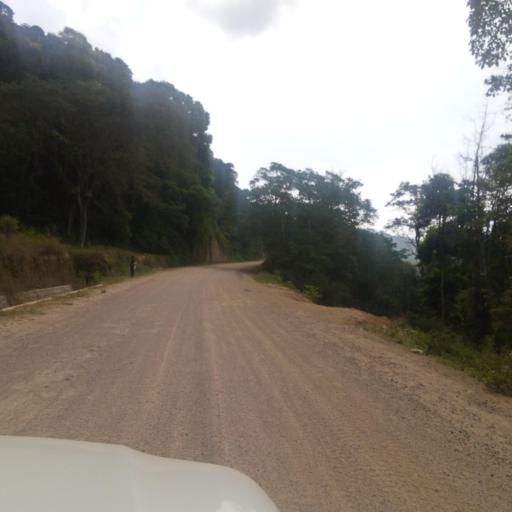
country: ET
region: Southern Nations, Nationalities, and People's Region
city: Tippi
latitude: 7.0486
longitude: 35.4402
